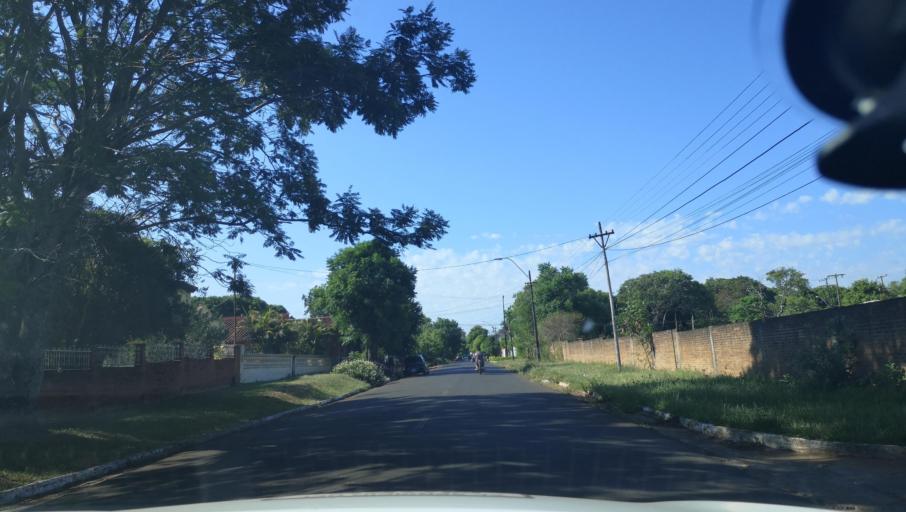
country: PY
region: Itapua
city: Carmen del Parana
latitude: -27.1589
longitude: -56.2367
